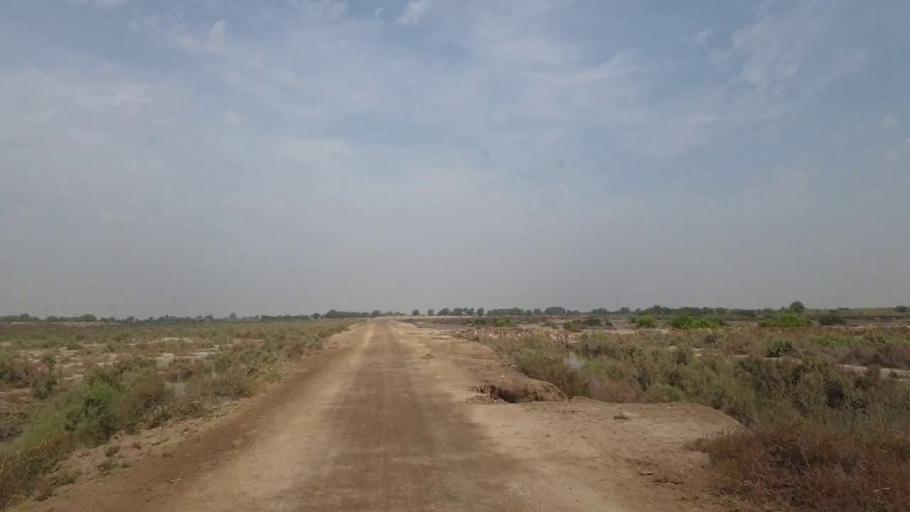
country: PK
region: Sindh
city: Rajo Khanani
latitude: 24.9941
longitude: 68.9952
